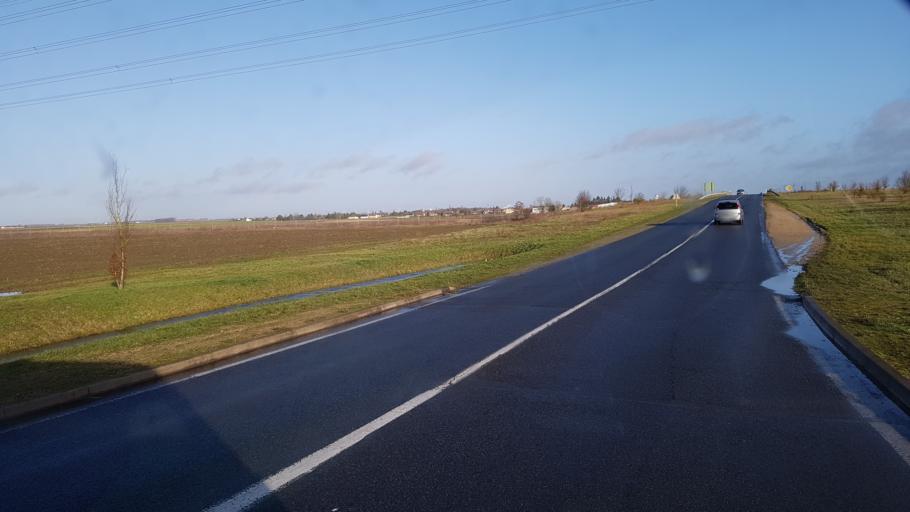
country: FR
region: Centre
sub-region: Departement du Loiret
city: Dadonville
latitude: 48.1111
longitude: 2.2478
